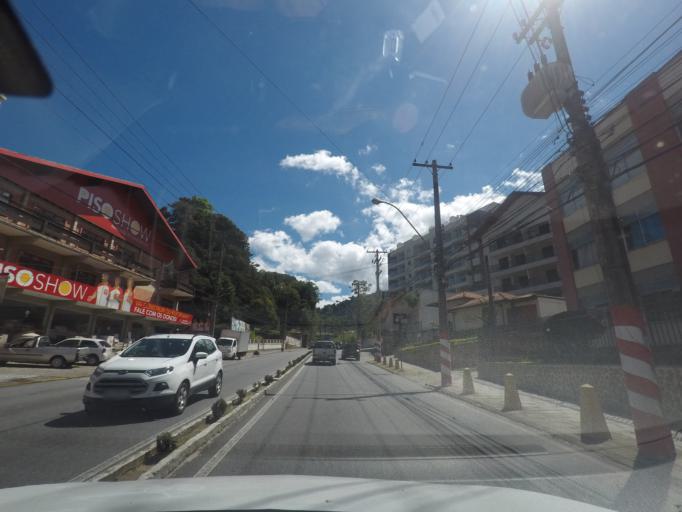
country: BR
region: Rio de Janeiro
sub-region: Teresopolis
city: Teresopolis
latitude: -22.4262
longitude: -42.9799
